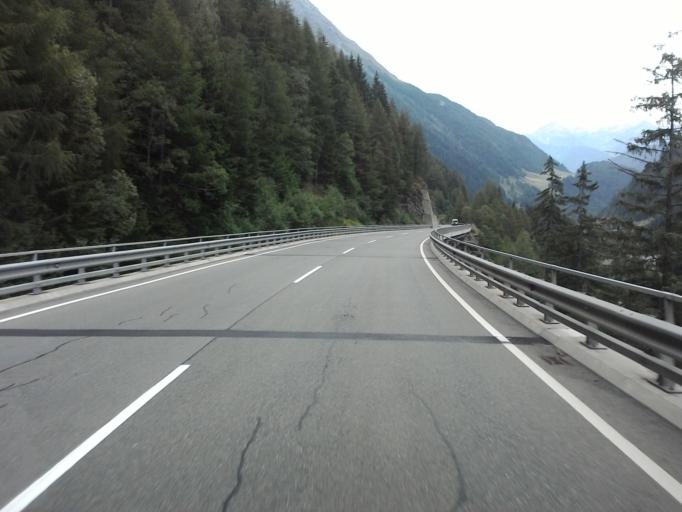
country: AT
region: Tyrol
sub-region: Politischer Bezirk Lienz
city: Matrei in Osttirol
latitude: 47.0838
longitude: 12.5305
